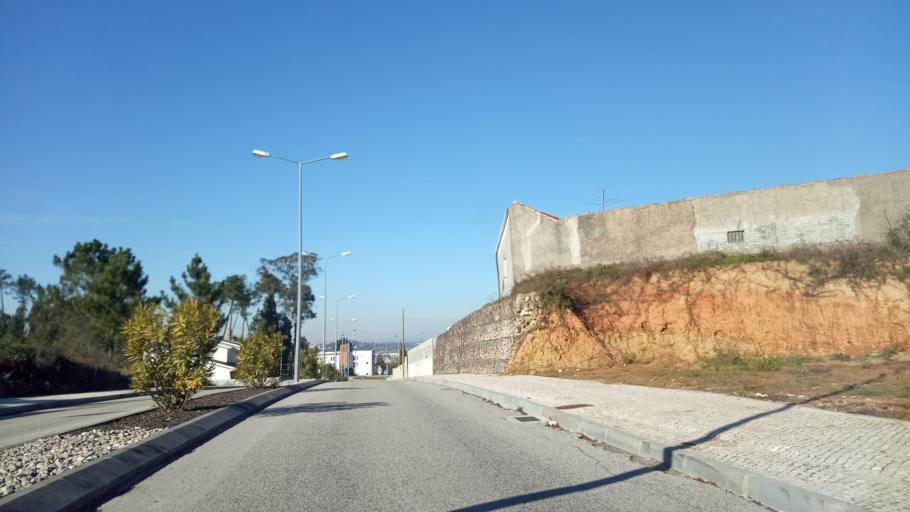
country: PT
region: Aveiro
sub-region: Anadia
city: Anadia
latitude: 40.4382
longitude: -8.4428
